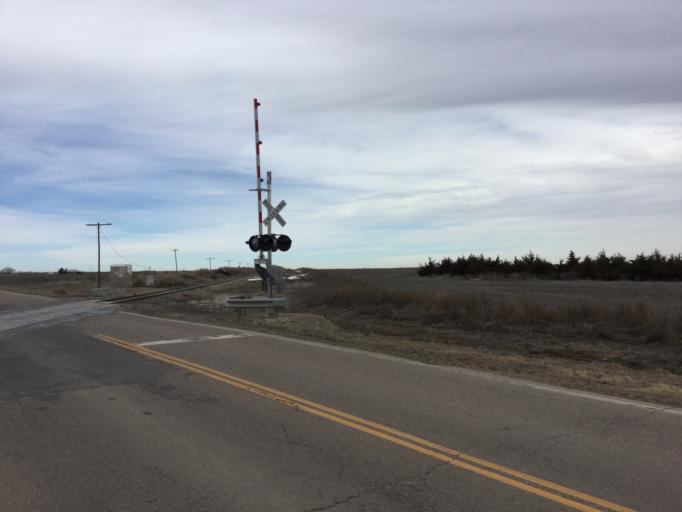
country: US
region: Kansas
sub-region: Lane County
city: Dighton
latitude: 38.4815
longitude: -100.4051
